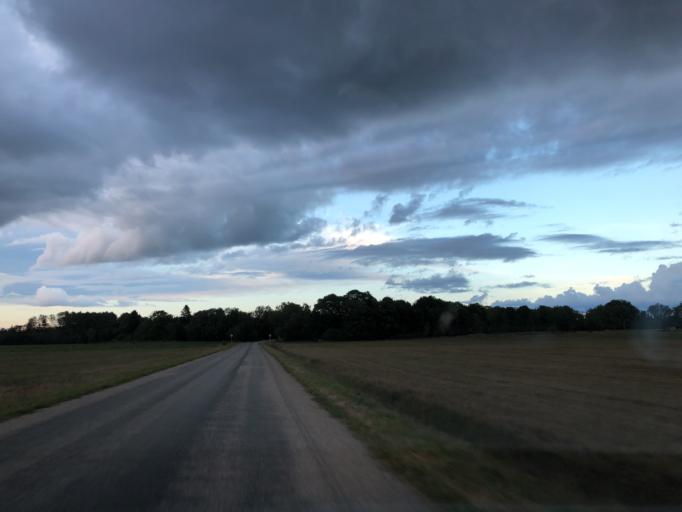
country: EE
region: Laeaene
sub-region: Ridala Parish
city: Uuemoisa
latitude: 58.8770
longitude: 23.6263
